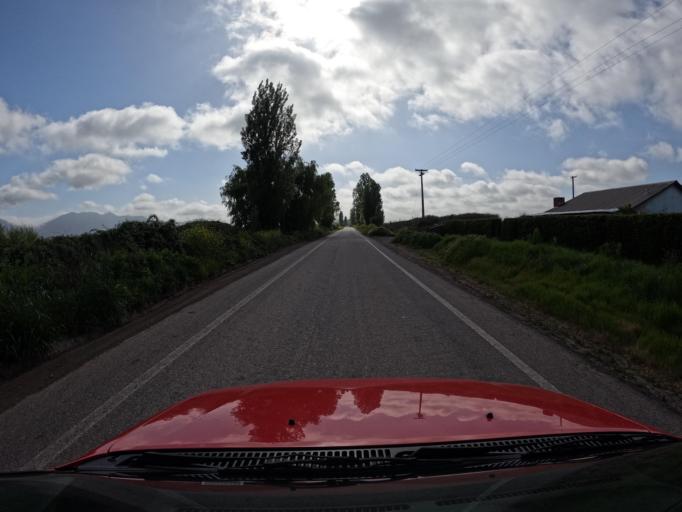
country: CL
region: Maule
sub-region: Provincia de Curico
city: Rauco
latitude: -34.8846
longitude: -71.2529
